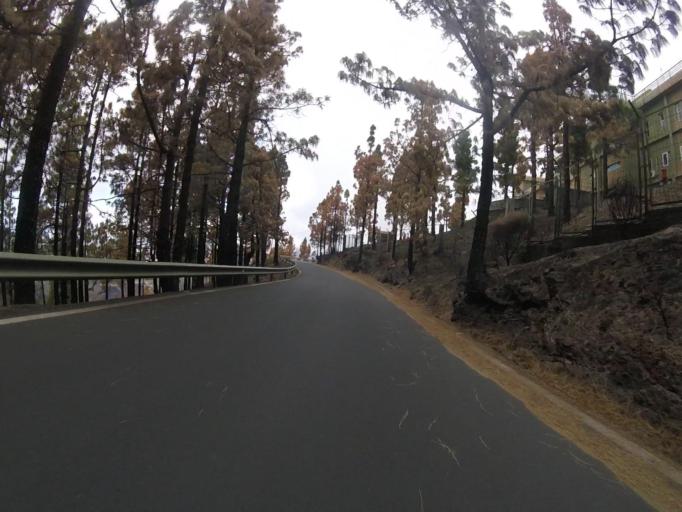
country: ES
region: Canary Islands
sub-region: Provincia de Las Palmas
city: San Bartolome
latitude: 27.9631
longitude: -15.5721
